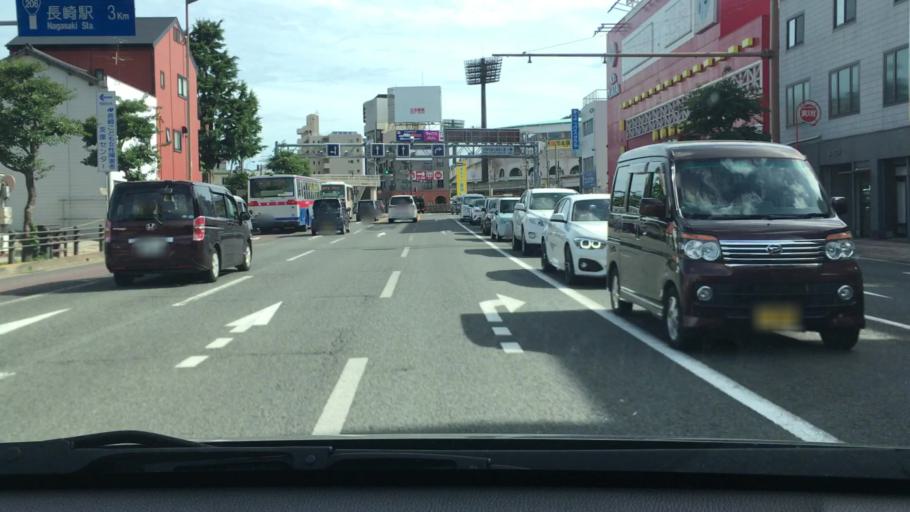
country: JP
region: Nagasaki
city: Nagasaki-shi
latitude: 32.7795
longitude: 129.8620
